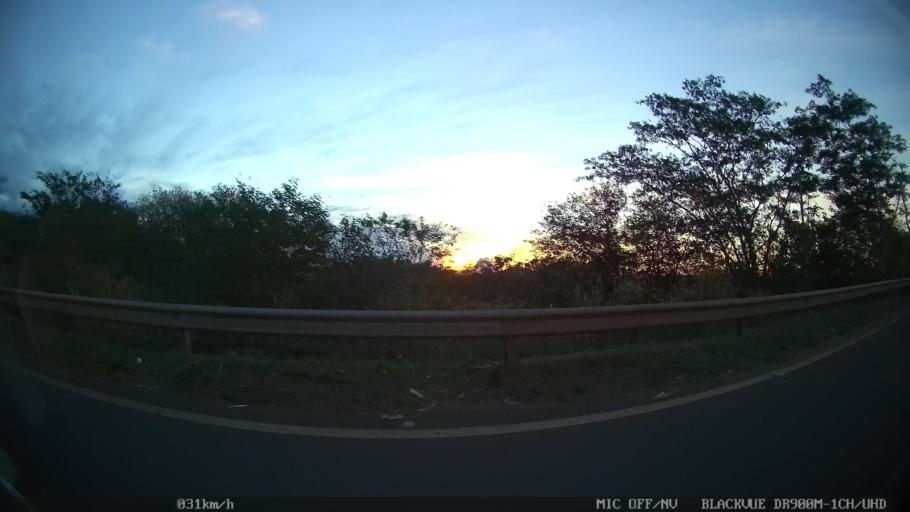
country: BR
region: Sao Paulo
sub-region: Catanduva
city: Catanduva
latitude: -21.1075
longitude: -48.9615
